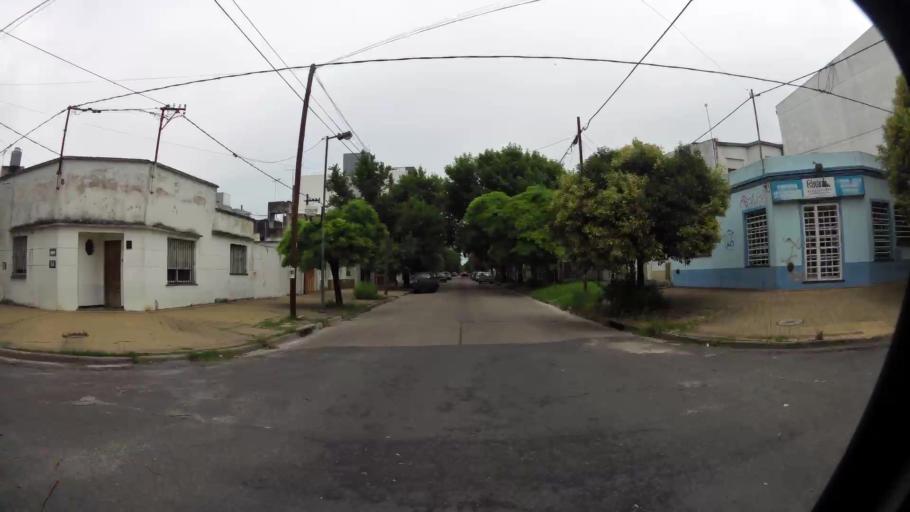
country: AR
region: Buenos Aires
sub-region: Partido de La Plata
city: La Plata
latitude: -34.9296
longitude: -57.9687
